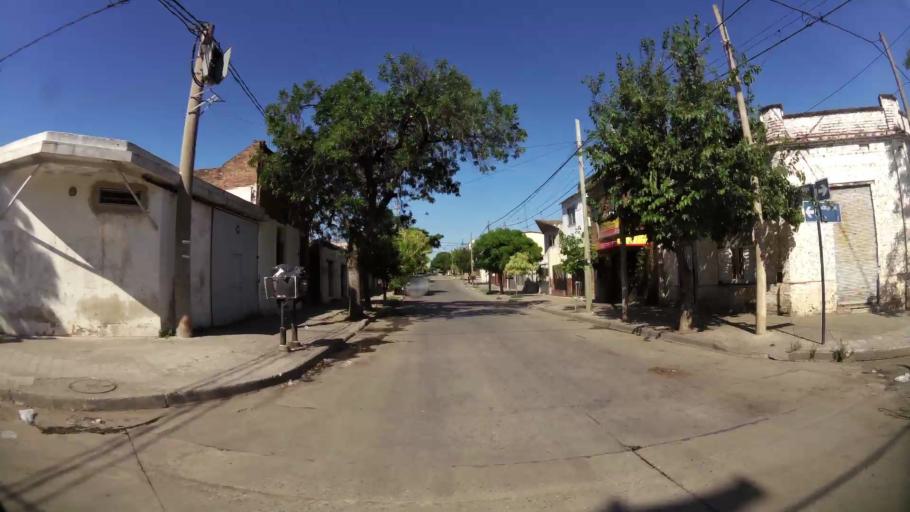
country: AR
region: Cordoba
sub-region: Departamento de Capital
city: Cordoba
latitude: -31.4106
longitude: -64.1504
